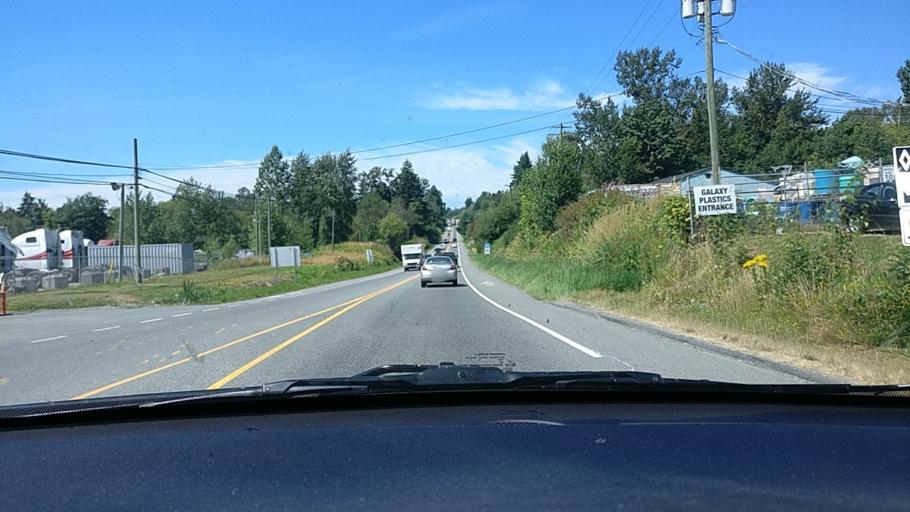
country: CA
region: British Columbia
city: Aldergrove
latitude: 49.0562
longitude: -122.3847
